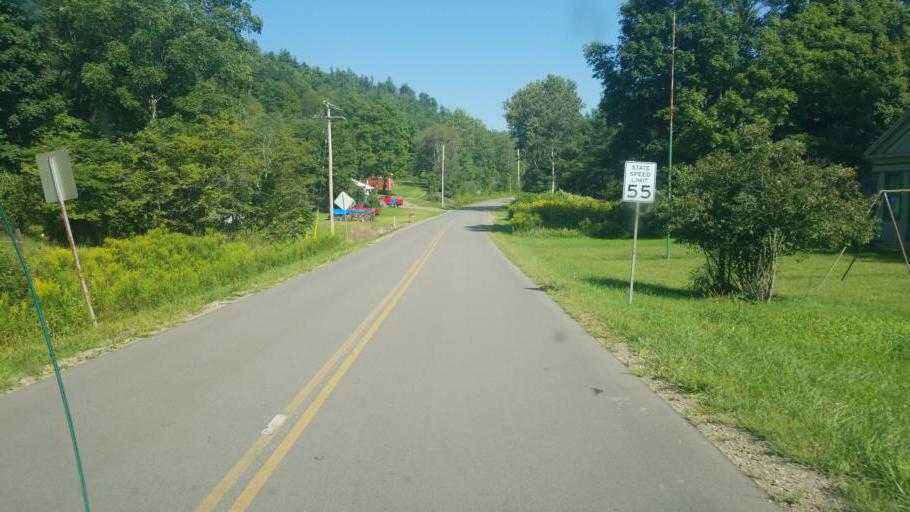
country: US
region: New York
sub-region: Allegany County
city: Bolivar
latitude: 42.0121
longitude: -78.0507
